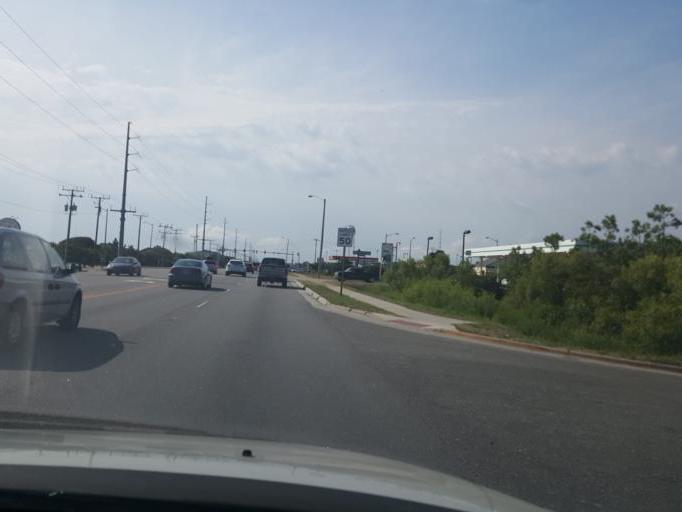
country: US
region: North Carolina
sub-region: Dare County
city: Kill Devil Hills
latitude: 36.0360
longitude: -75.6743
